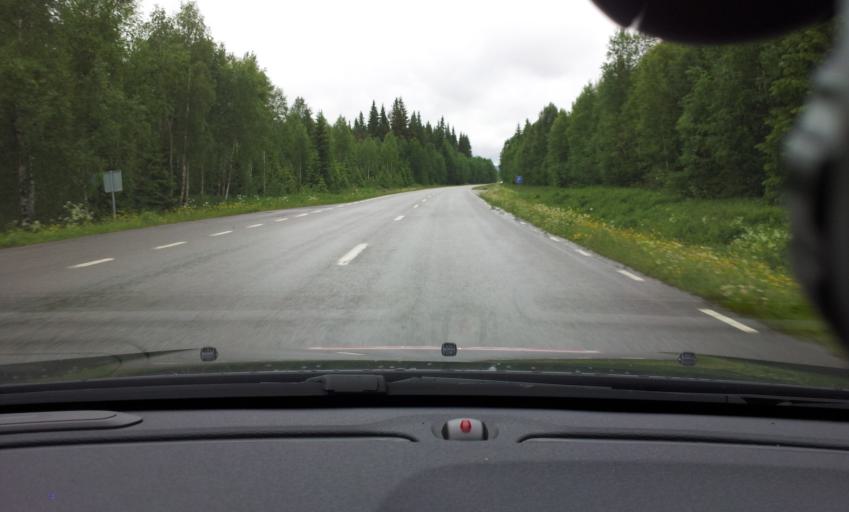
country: SE
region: Jaemtland
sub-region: Krokoms Kommun
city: Krokom
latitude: 63.3765
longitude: 14.5058
